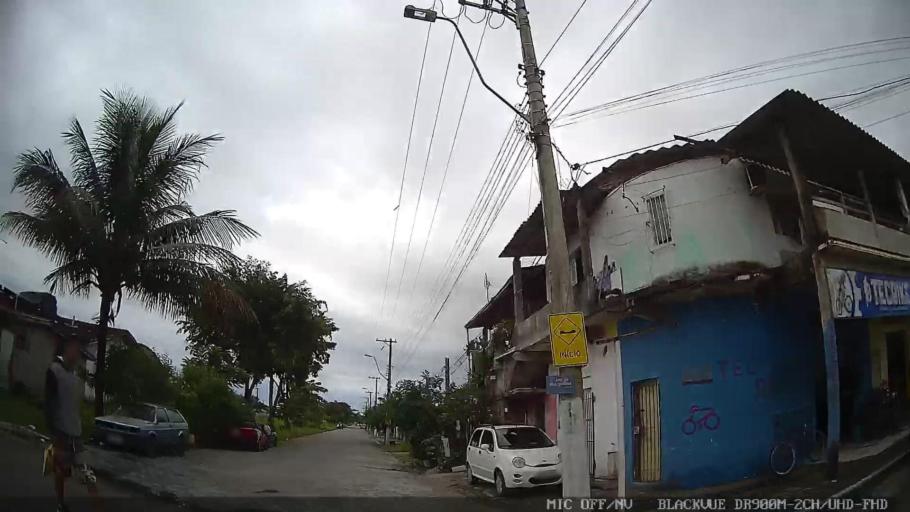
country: BR
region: Sao Paulo
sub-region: Sao Sebastiao
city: Sao Sebastiao
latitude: -23.7098
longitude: -45.4427
